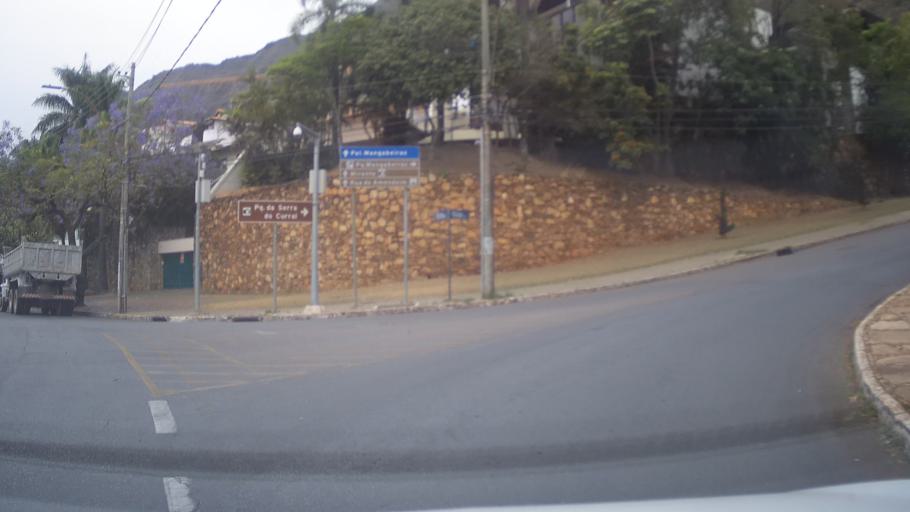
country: BR
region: Minas Gerais
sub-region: Belo Horizonte
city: Belo Horizonte
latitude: -19.9583
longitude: -43.9145
